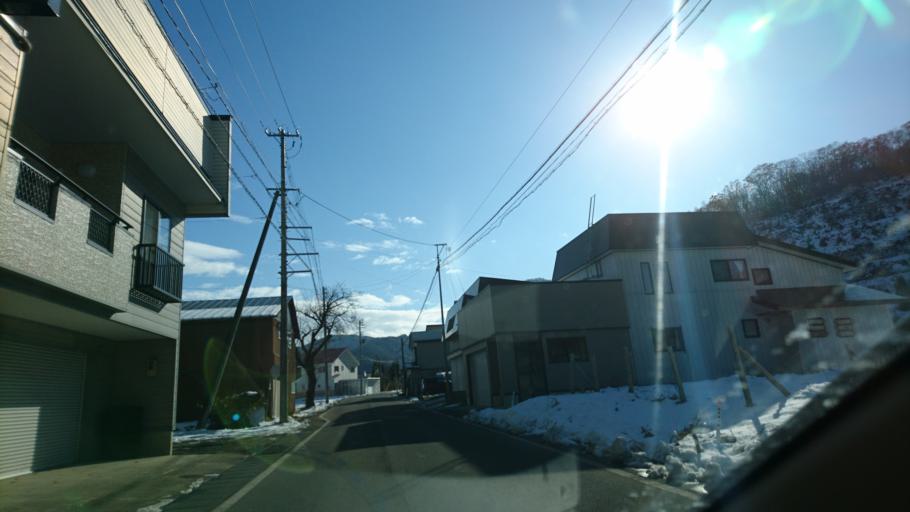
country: JP
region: Akita
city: Yokotemachi
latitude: 39.3100
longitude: 140.7781
